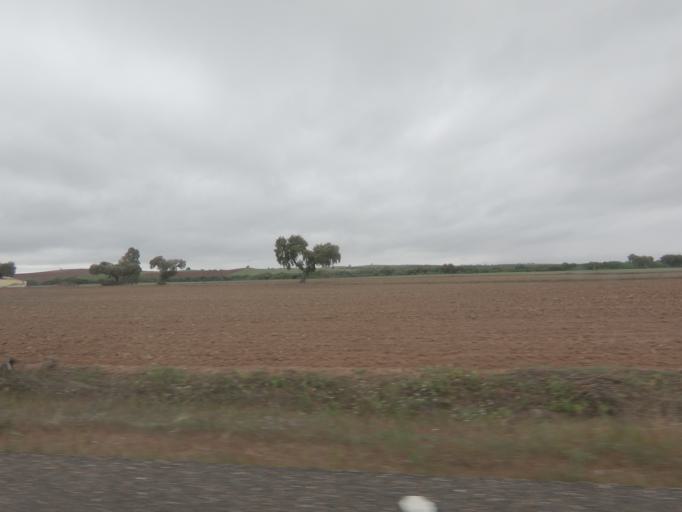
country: ES
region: Extremadura
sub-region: Provincia de Badajoz
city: La Roca de la Sierra
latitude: 39.0613
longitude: -6.7674
